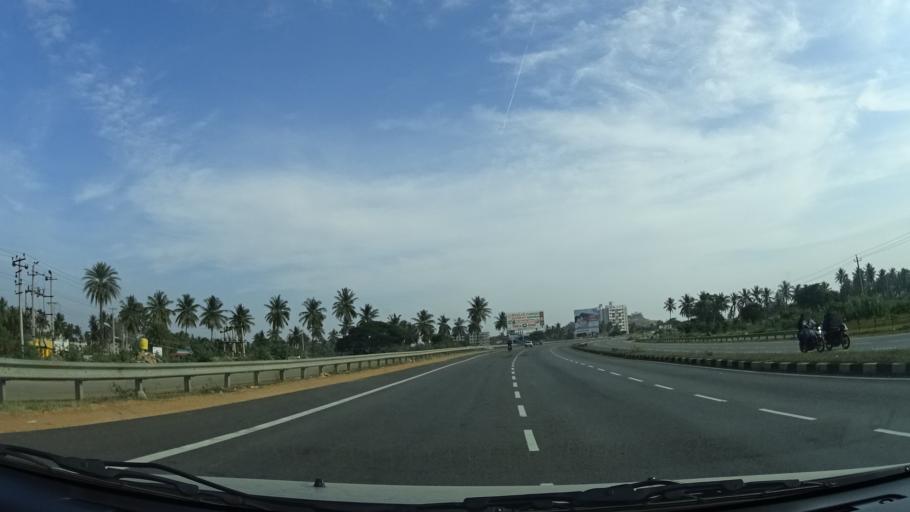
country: IN
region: Karnataka
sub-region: Bangalore Rural
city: Devanhalli
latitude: 13.2524
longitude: 77.7074
